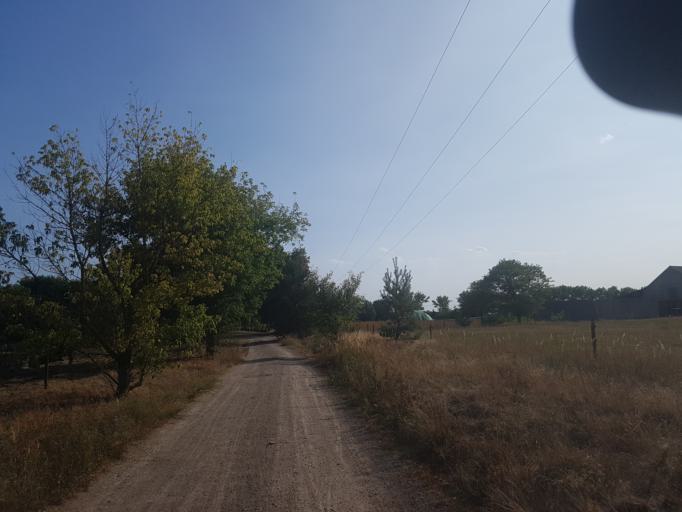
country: DE
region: Saxony-Anhalt
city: Jessen
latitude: 51.8590
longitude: 13.0319
